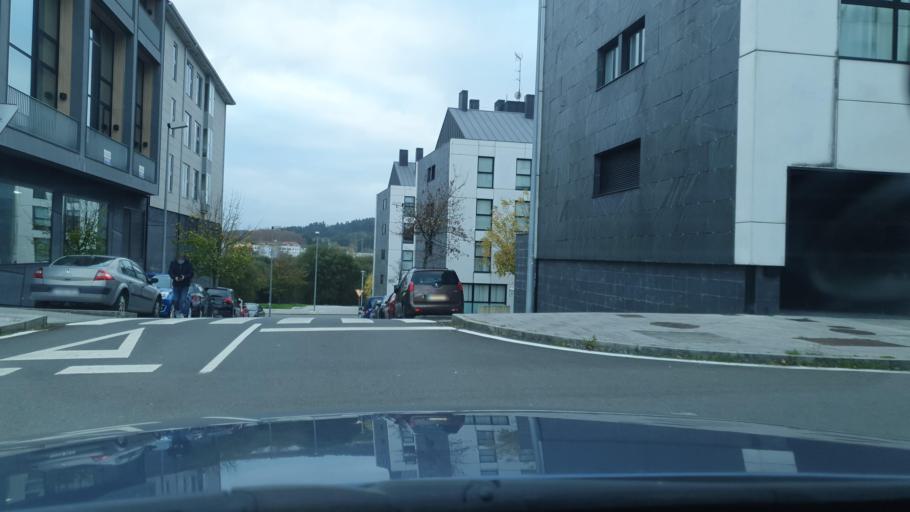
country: ES
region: Galicia
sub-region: Provincia da Coruna
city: Santiago de Compostela
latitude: 42.8659
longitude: -8.5639
